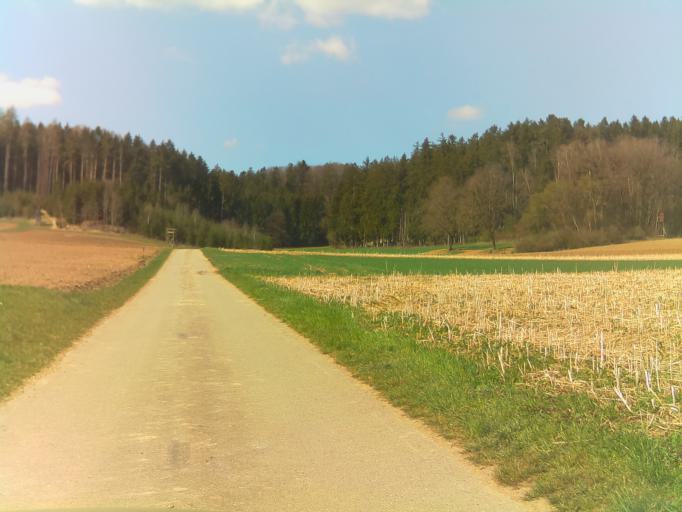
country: DE
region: Bavaria
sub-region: Swabia
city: Biberbach
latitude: 48.4899
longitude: 10.8174
